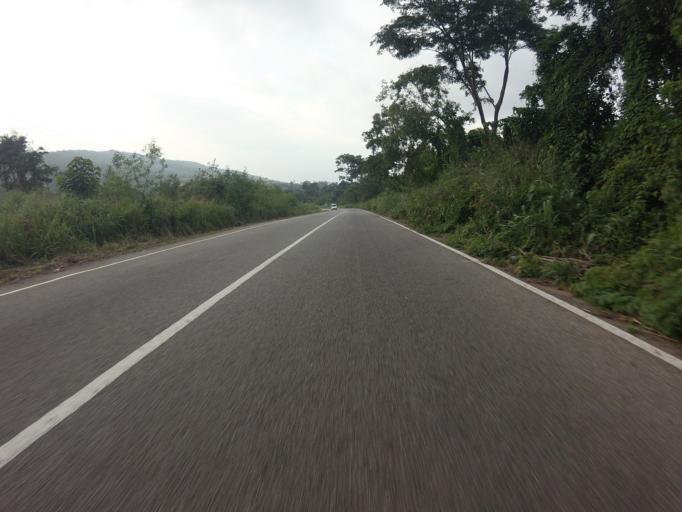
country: GH
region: Volta
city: Ho
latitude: 6.6463
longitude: 0.4698
